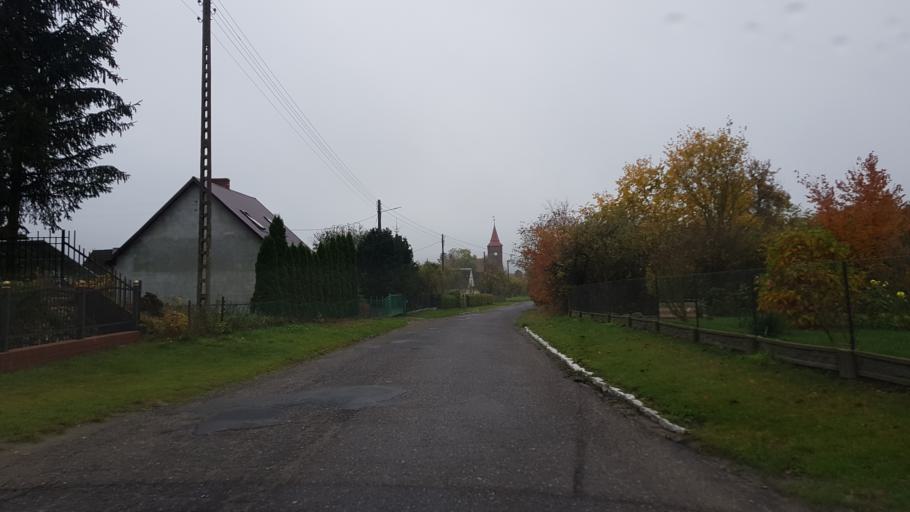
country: PL
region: West Pomeranian Voivodeship
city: Trzcinsko Zdroj
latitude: 53.0624
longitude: 14.5350
